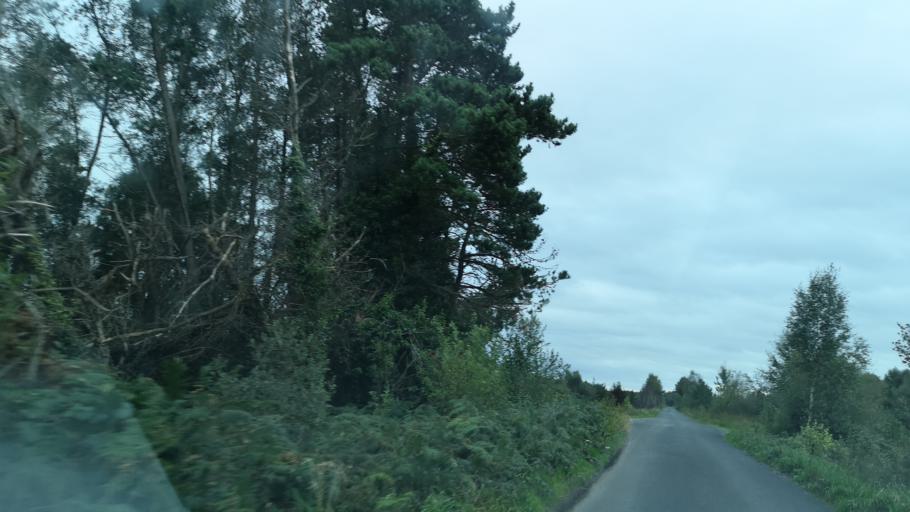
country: IE
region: Leinster
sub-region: Uibh Fhaili
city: Ferbane
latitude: 53.2082
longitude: -7.7236
